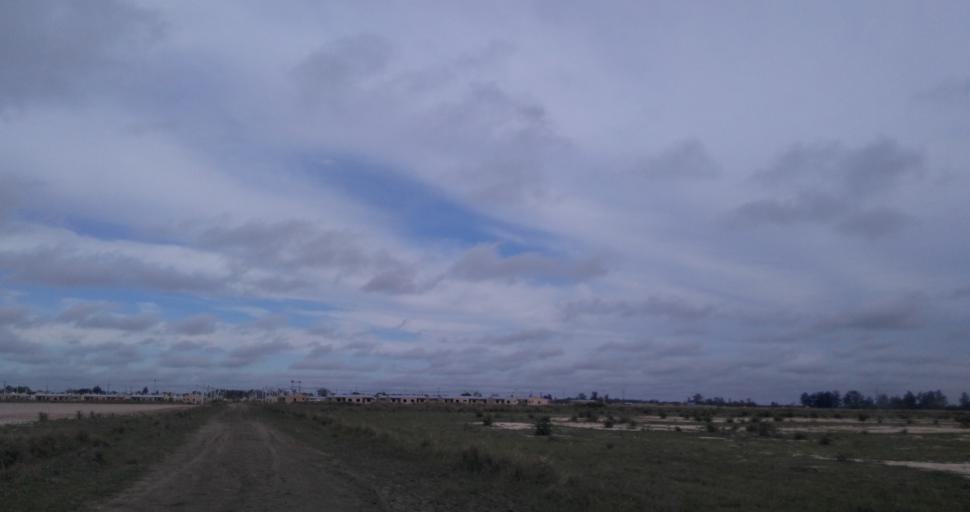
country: AR
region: Chaco
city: Fontana
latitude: -27.3922
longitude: -58.9852
